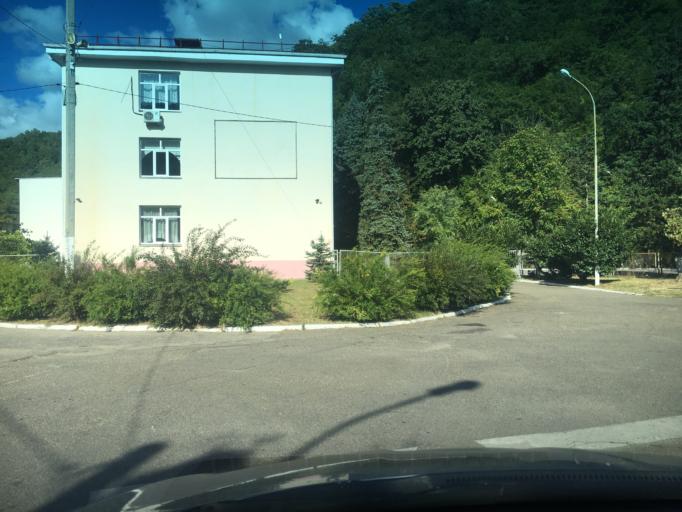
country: RU
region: Krasnodarskiy
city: Nebug
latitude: 44.1864
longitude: 38.9738
